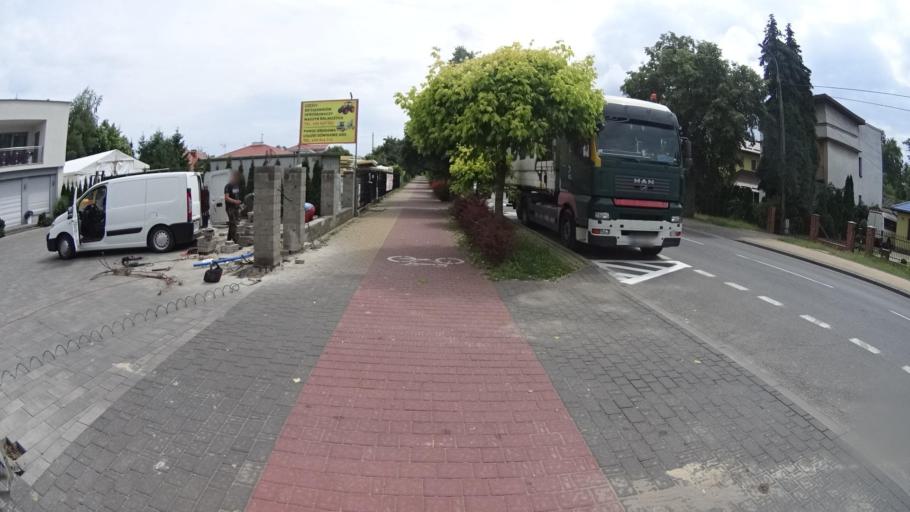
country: PL
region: Masovian Voivodeship
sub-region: Powiat grojecki
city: Grojec
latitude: 51.8583
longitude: 20.8692
